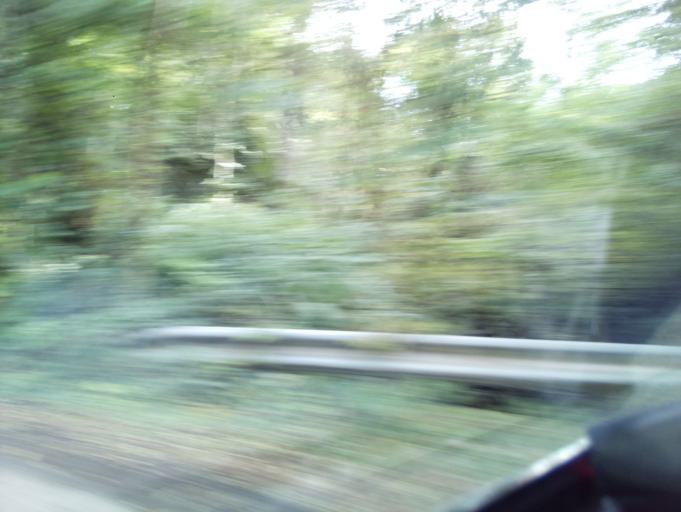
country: GB
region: Wales
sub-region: Cardiff
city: Pentyrch
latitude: 51.5612
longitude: -3.2839
